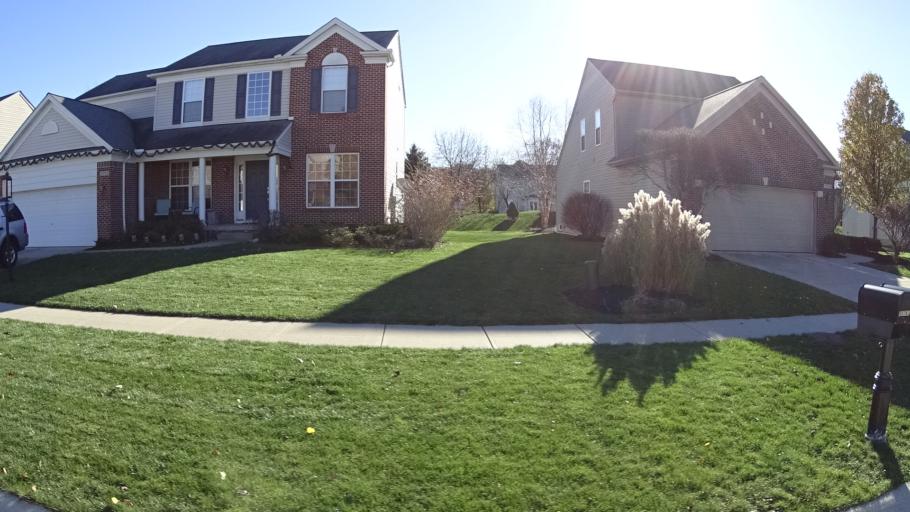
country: US
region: Ohio
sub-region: Lorain County
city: Avon Center
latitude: 41.4523
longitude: -82.0139
